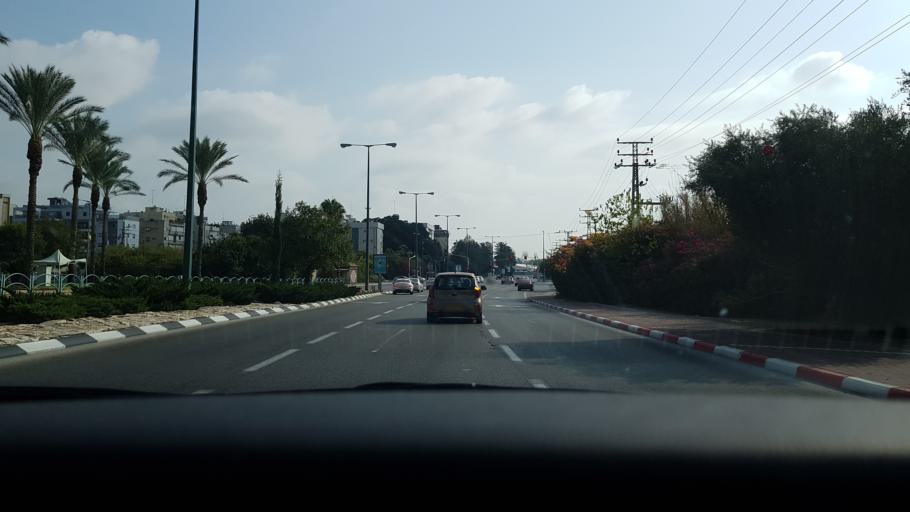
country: IL
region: Central District
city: Ness Ziona
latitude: 31.9238
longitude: 34.7932
